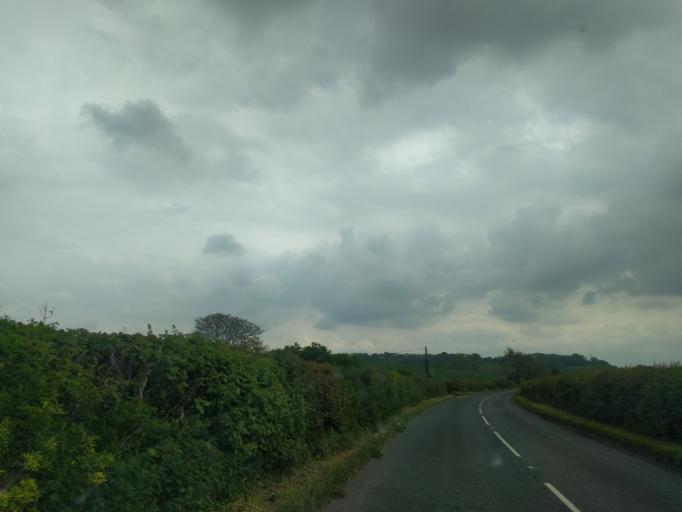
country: GB
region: England
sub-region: Somerset
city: Ilchester
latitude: 51.0609
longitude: -2.7087
